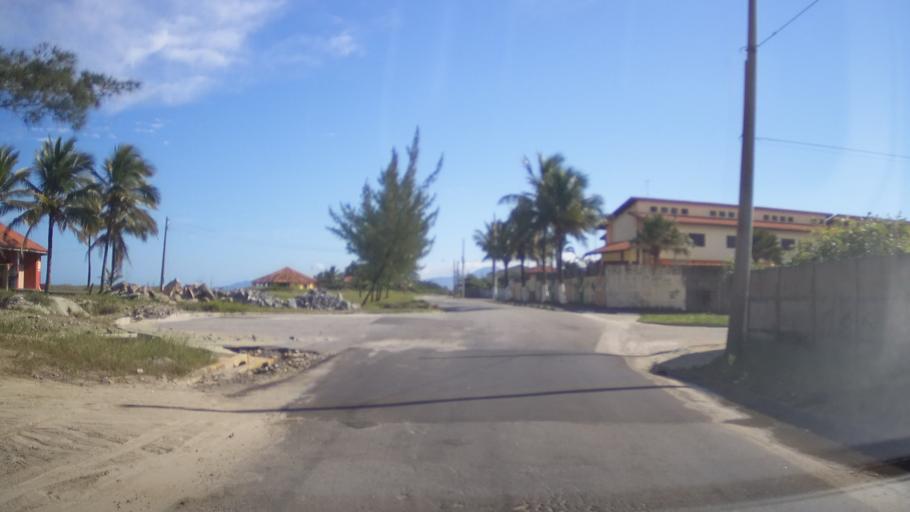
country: BR
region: Sao Paulo
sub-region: Itanhaem
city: Itanhaem
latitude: -24.2232
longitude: -46.8553
